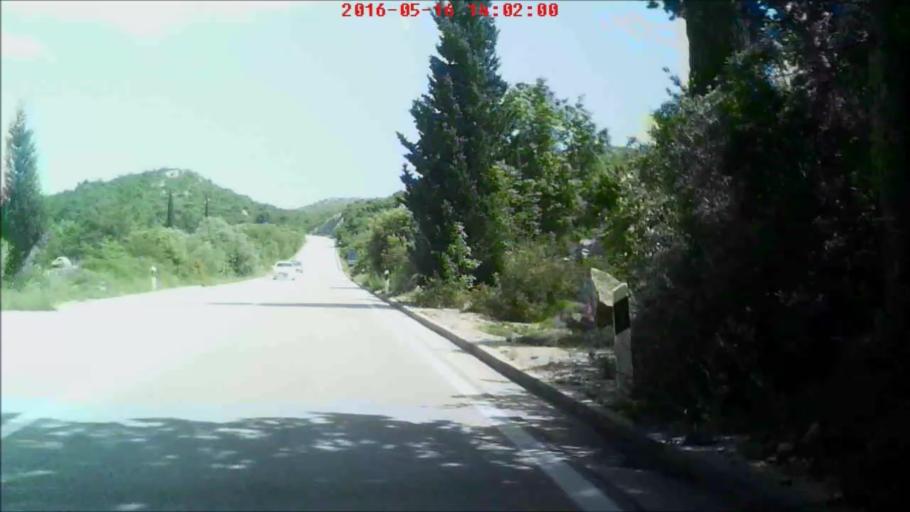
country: HR
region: Dubrovacko-Neretvanska
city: Ston
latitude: 42.8286
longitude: 17.7540
